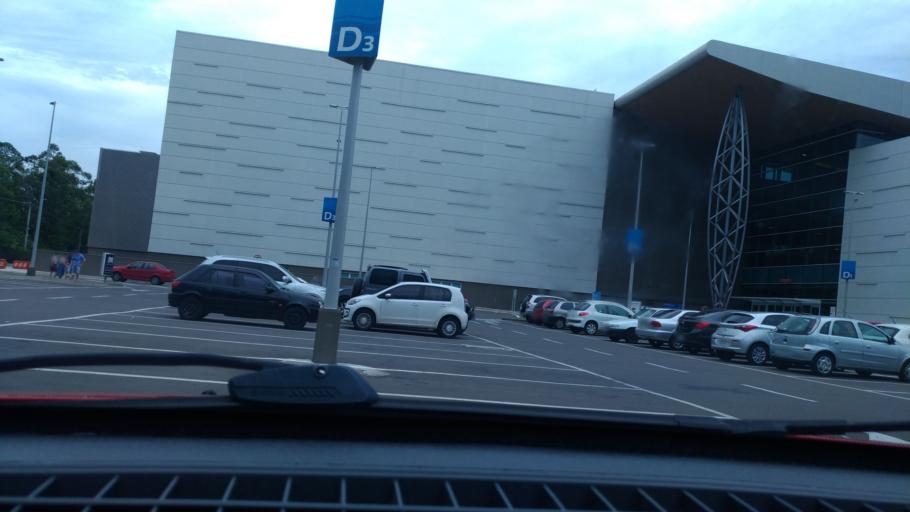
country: BR
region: Rio Grande do Sul
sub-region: Canoas
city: Canoas
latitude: -29.9137
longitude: -51.1639
